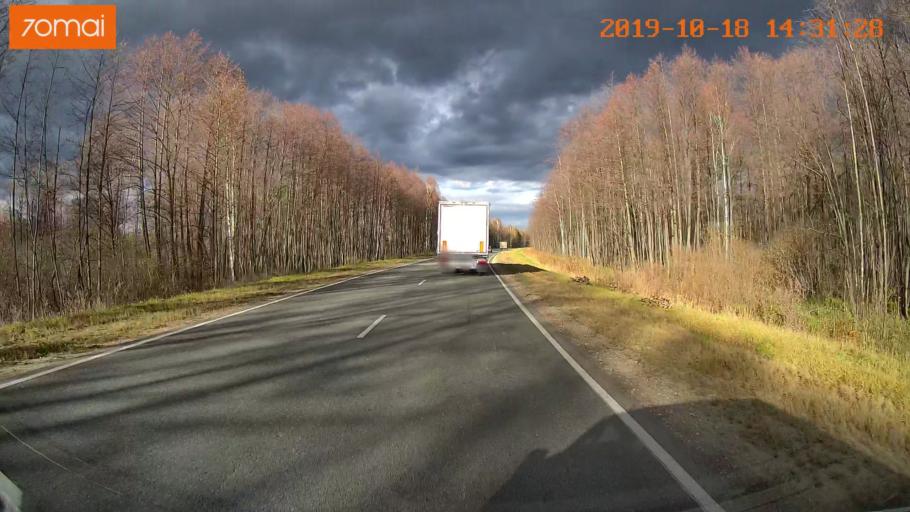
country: RU
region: Rjazan
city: Tuma
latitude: 55.1829
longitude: 40.5702
